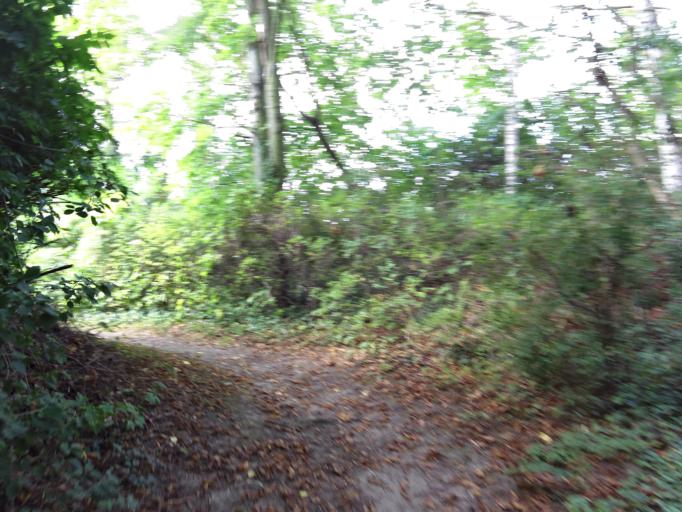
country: DE
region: Saxony
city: Leipzig
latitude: 51.3802
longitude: 12.3386
